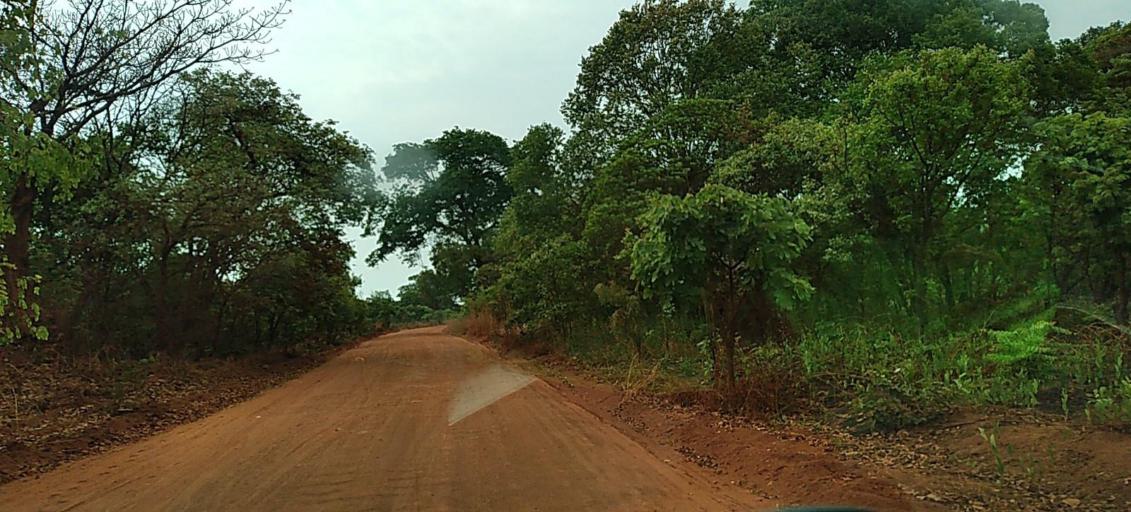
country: ZM
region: North-Western
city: Solwezi
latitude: -12.2168
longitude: 26.5076
